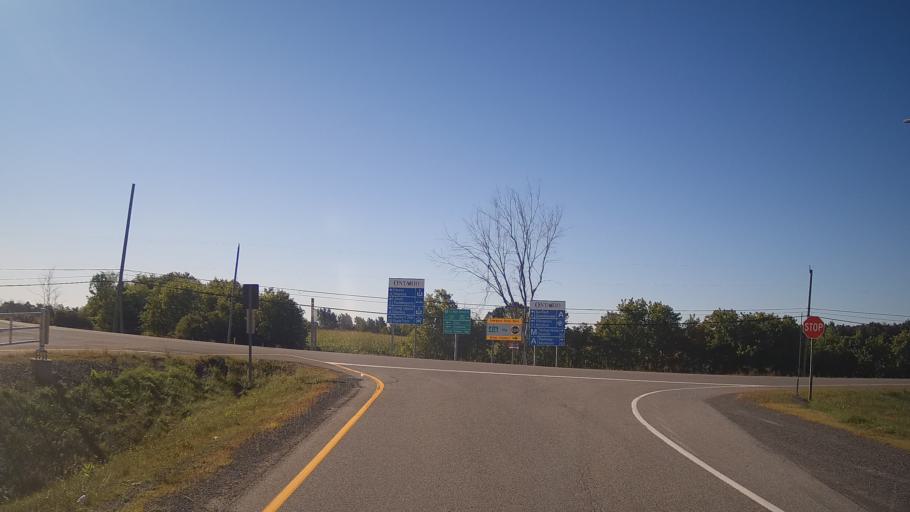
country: CA
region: Ontario
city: Bells Corners
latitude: 45.1455
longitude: -75.6828
